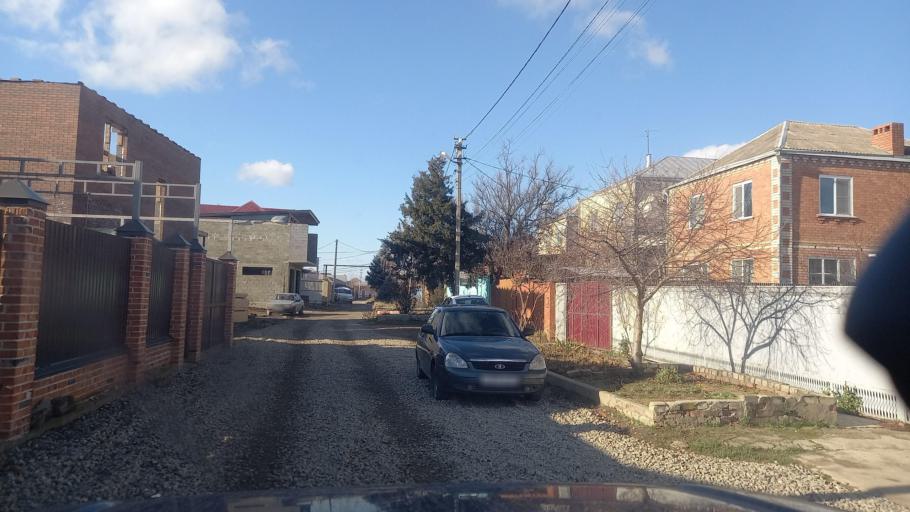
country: RU
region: Adygeya
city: Yablonovskiy
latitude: 44.9932
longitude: 38.9415
